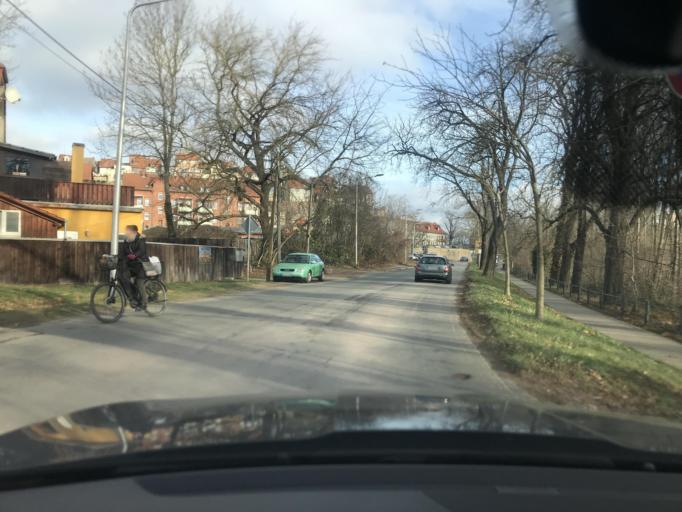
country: DE
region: Saxony-Anhalt
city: Quedlinburg
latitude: 51.7854
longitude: 11.1300
